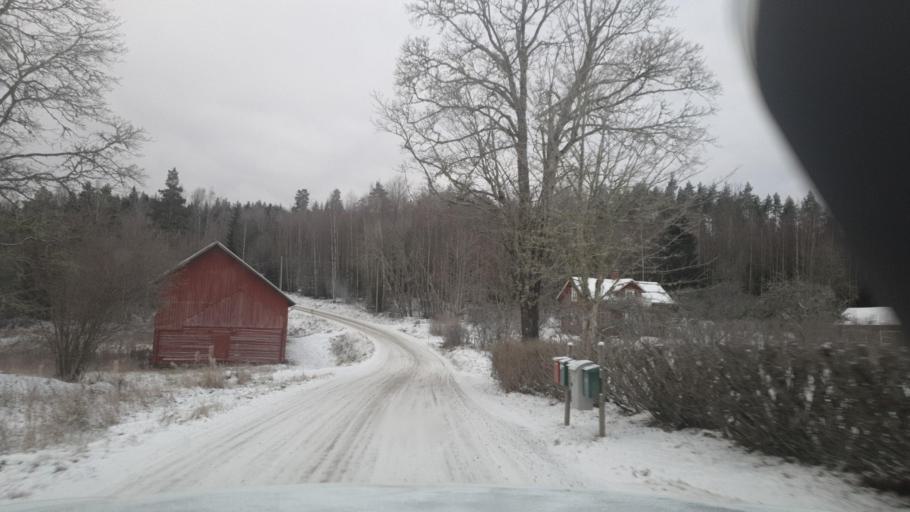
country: SE
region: Vaermland
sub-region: Grums Kommun
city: Grums
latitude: 59.4773
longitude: 12.9291
